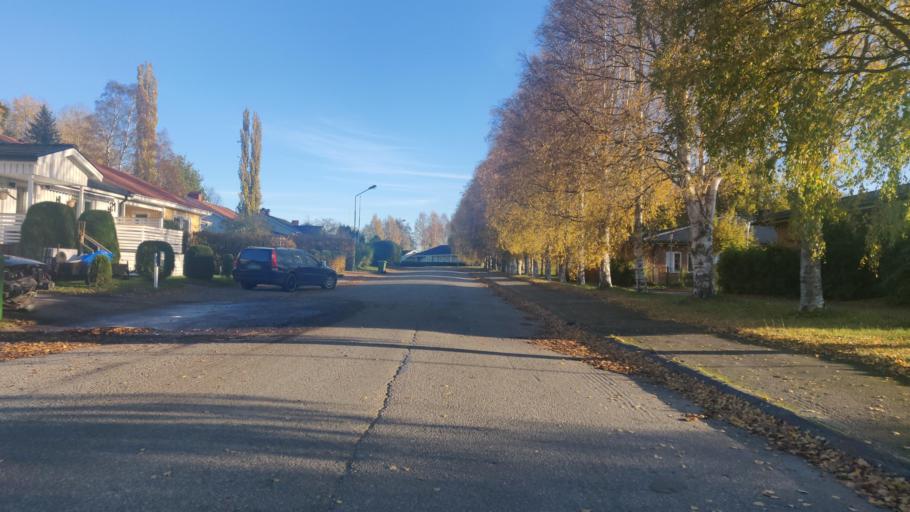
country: SE
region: Vaesternorrland
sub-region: Sundsvalls Kommun
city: Skottsund
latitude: 62.2909
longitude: 17.3900
